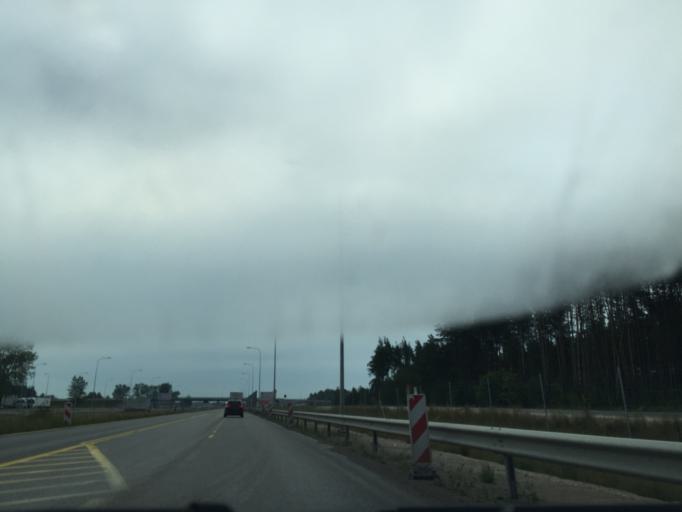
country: PL
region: Podlasie
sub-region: Powiat zambrowski
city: Szumowo
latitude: 52.9074
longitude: 22.0932
